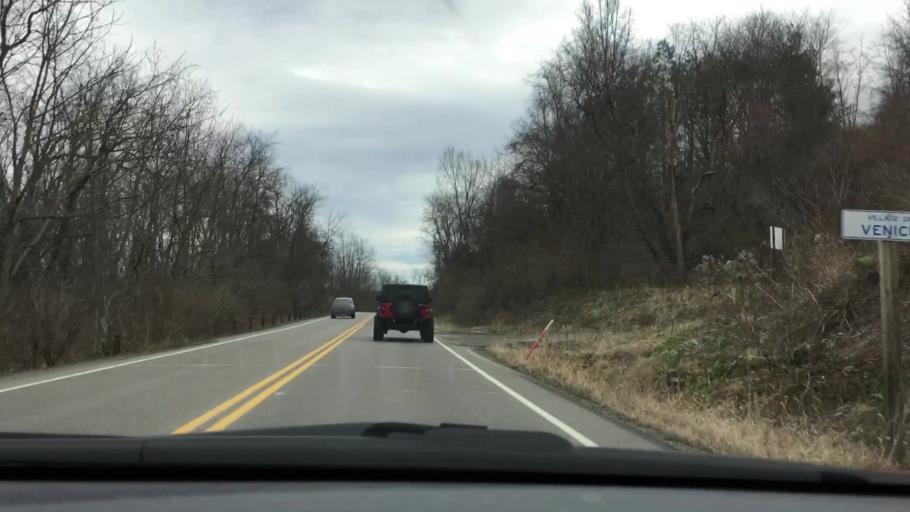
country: US
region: Pennsylvania
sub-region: Washington County
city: Cecil-Bishop
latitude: 40.3271
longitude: -80.2348
